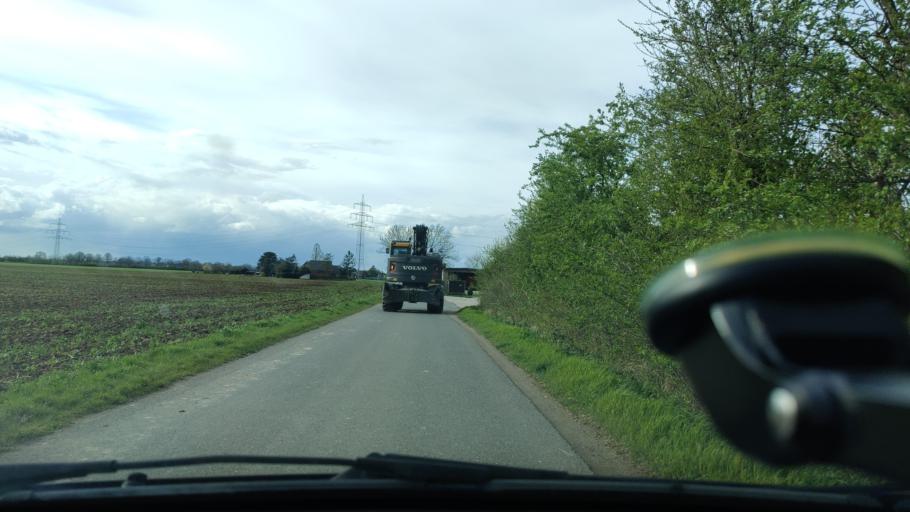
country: DE
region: North Rhine-Westphalia
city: Rees
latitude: 51.7356
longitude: 6.4104
